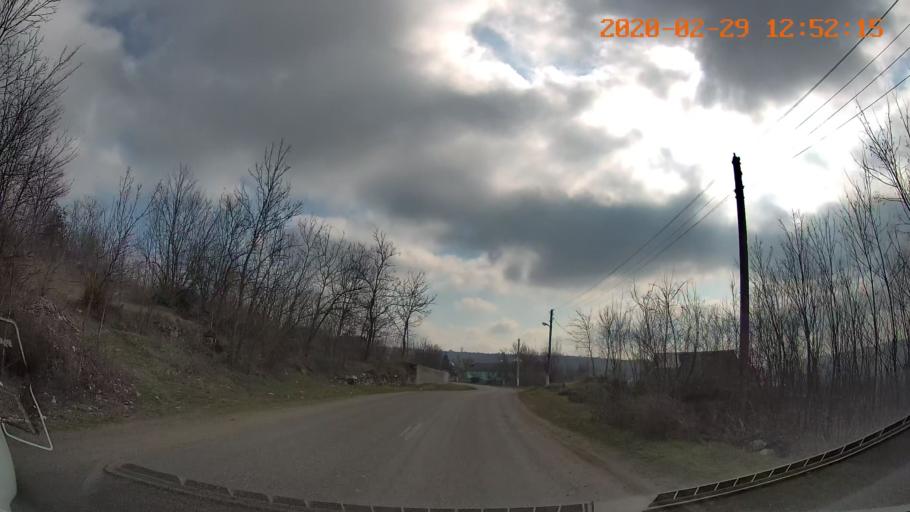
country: MD
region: Telenesti
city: Camenca
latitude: 48.1129
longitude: 28.7325
